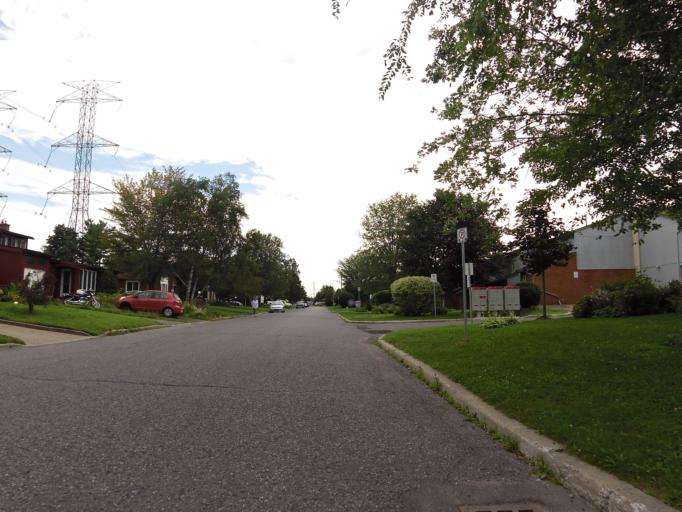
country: CA
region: Ontario
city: Ottawa
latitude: 45.3327
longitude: -75.7404
